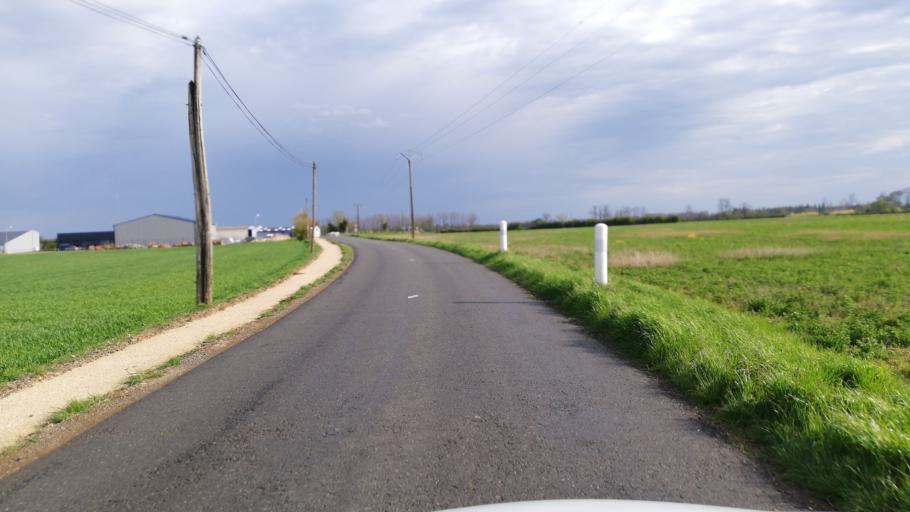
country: FR
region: Pays de la Loire
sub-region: Departement de la Vendee
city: Maillezais
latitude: 46.3226
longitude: -0.7291
